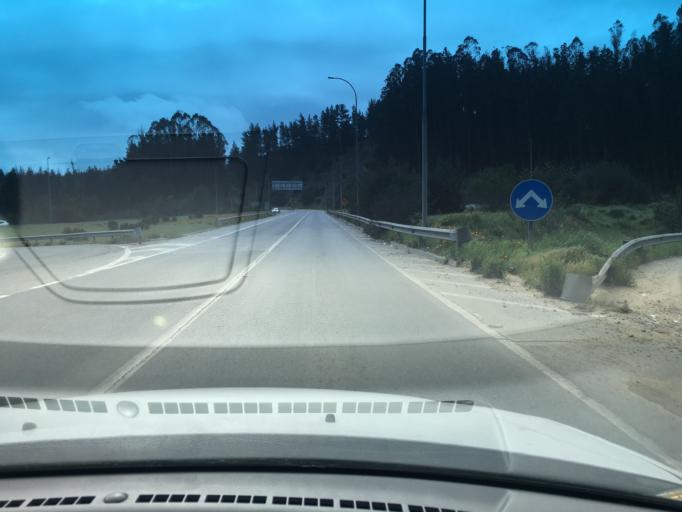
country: CL
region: Valparaiso
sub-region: Provincia de Valparaiso
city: Vina del Mar
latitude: -33.1081
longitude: -71.5558
